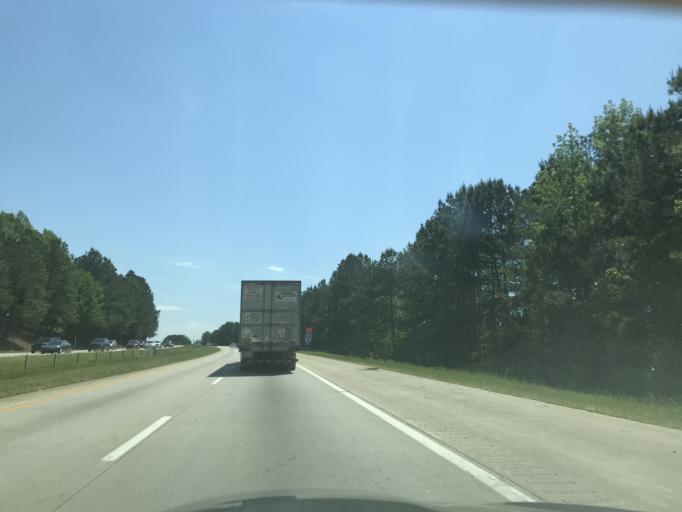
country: US
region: North Carolina
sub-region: Wake County
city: Garner
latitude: 35.6173
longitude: -78.5675
